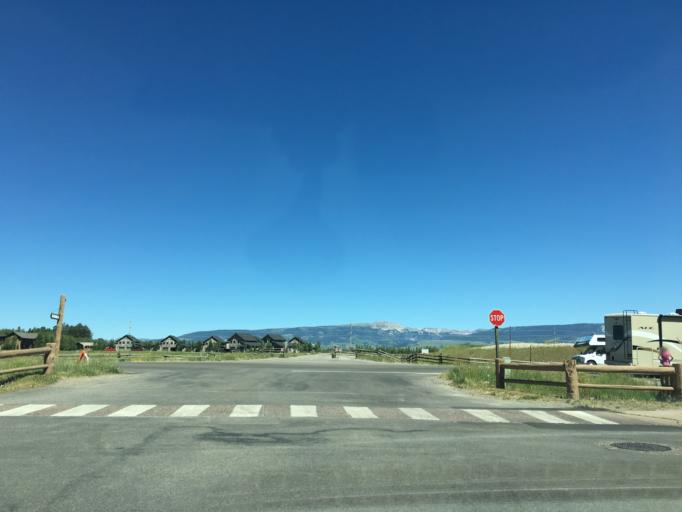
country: US
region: Wyoming
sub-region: Teton County
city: Moose Wilson Road
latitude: 43.5866
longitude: -110.8263
